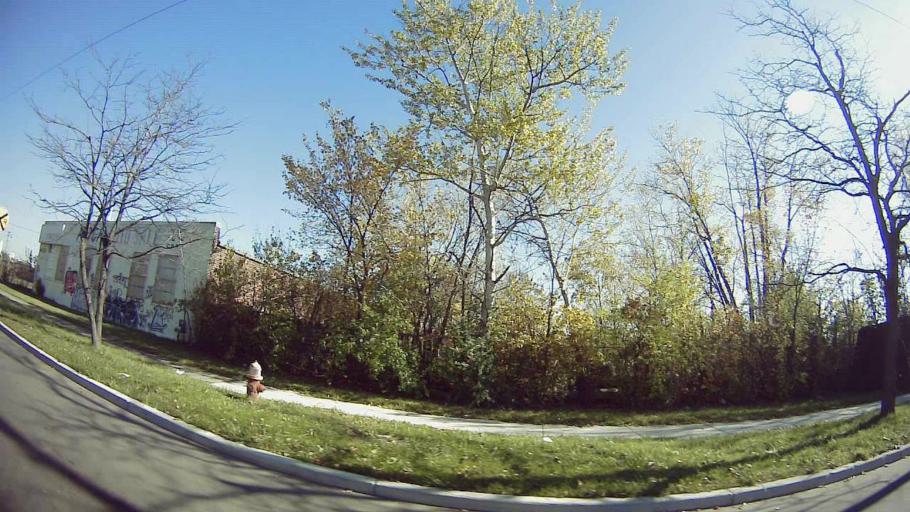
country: US
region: Michigan
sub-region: Wayne County
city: Dearborn
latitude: 42.3686
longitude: -83.1513
